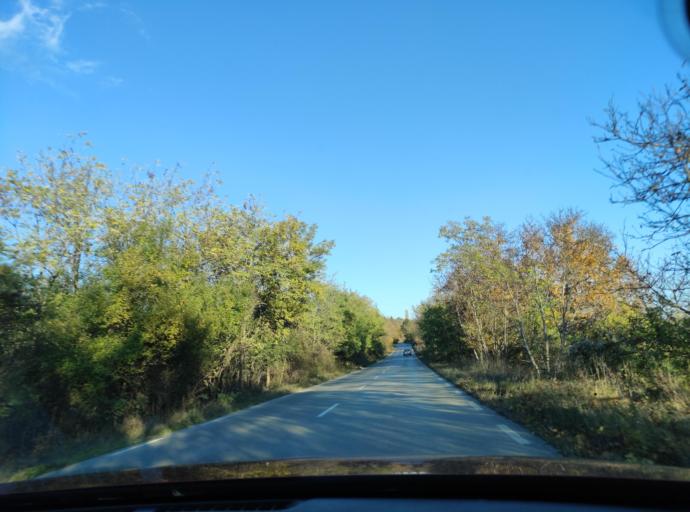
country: BG
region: Montana
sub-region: Obshtina Montana
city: Montana
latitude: 43.3956
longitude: 23.1231
